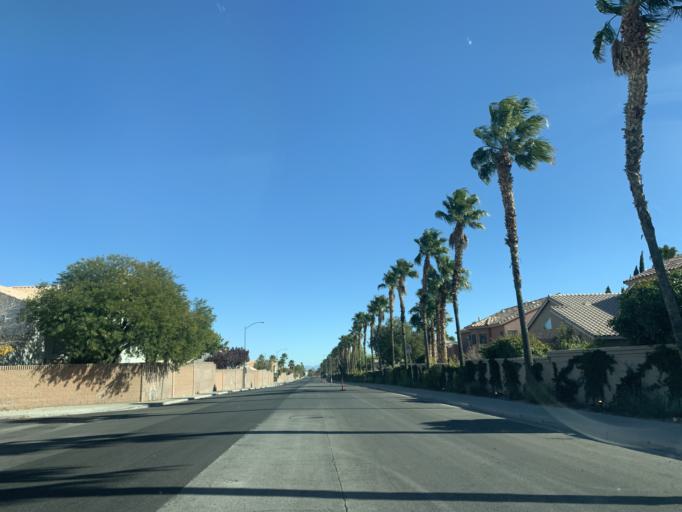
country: US
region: Nevada
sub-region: Clark County
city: Summerlin South
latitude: 36.1206
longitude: -115.3037
